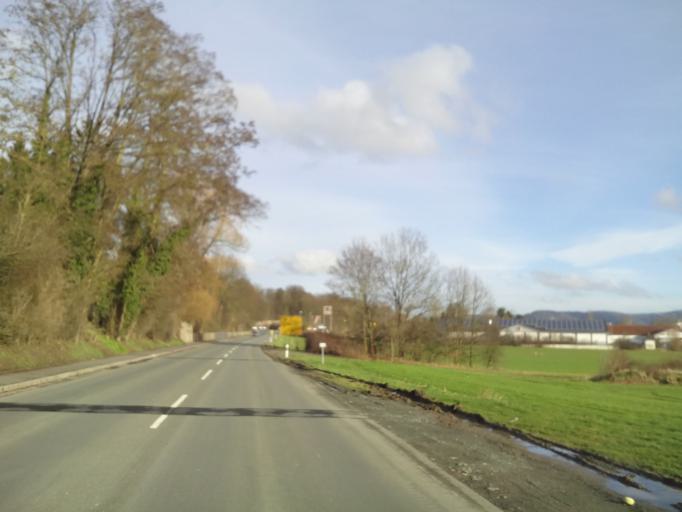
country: DE
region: Bavaria
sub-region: Upper Franconia
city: Mainleus
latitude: 50.1002
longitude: 11.3873
